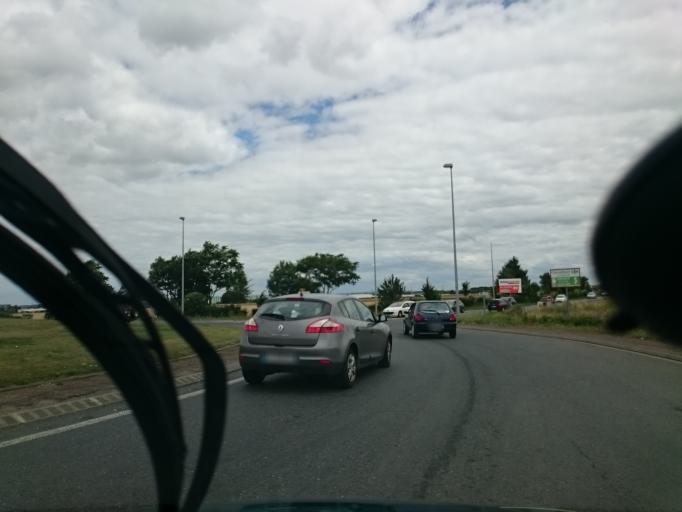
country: FR
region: Lower Normandy
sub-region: Departement du Calvados
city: Cormelles-le-Royal
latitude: 49.1469
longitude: -0.3193
